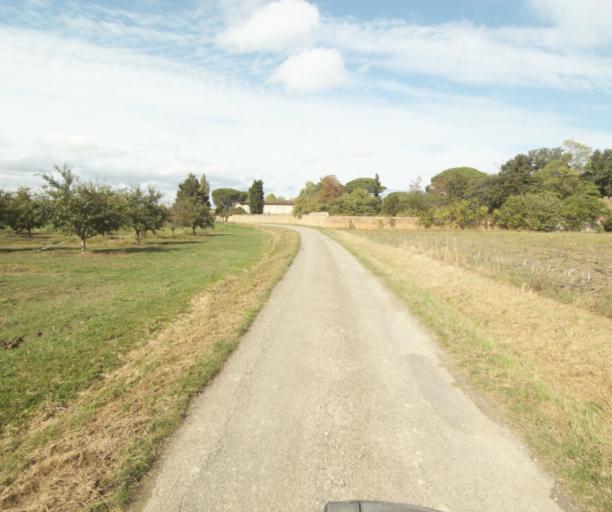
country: FR
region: Midi-Pyrenees
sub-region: Departement du Tarn-et-Garonne
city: Finhan
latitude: 43.8806
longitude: 1.1985
